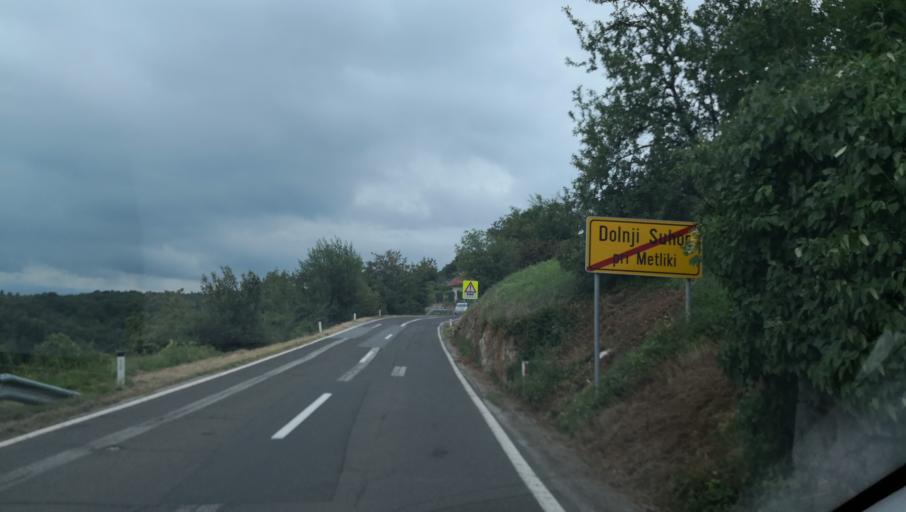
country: SI
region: Metlika
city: Metlika
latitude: 45.6894
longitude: 15.2728
